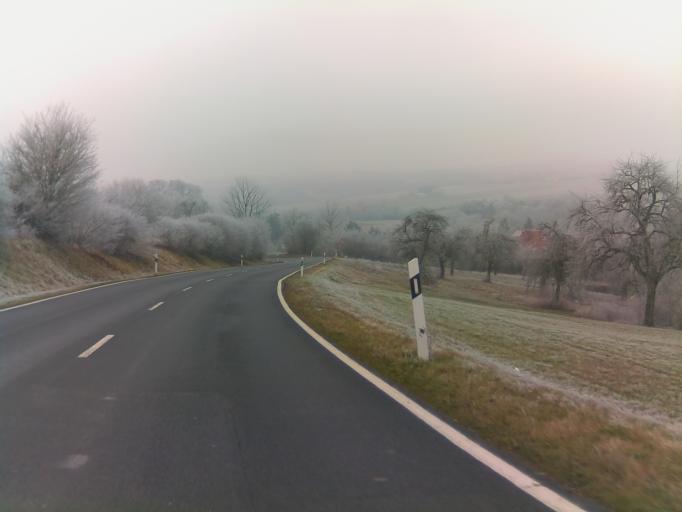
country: DE
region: Baden-Wuerttemberg
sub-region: Karlsruhe Region
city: Rosenberg
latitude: 49.4522
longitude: 9.4776
